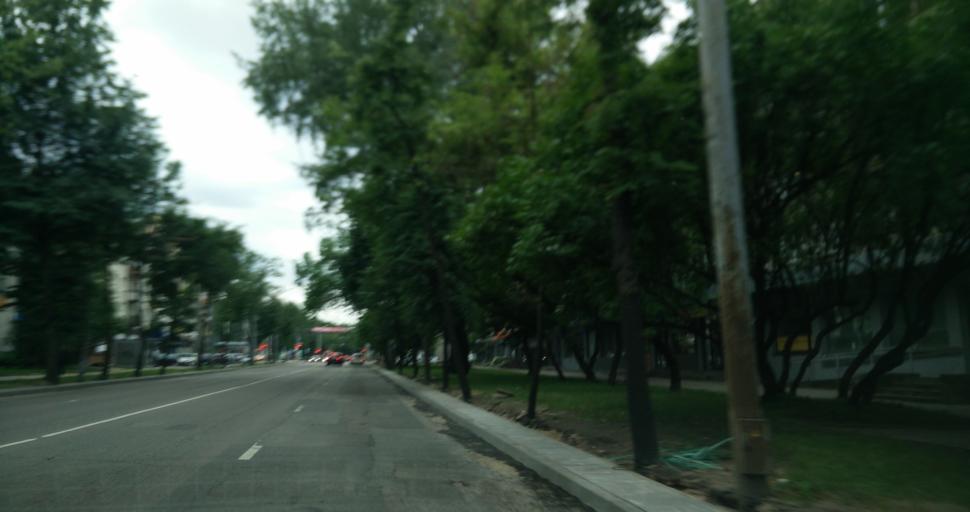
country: LT
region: Vilnius County
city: Rasos
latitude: 54.7131
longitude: 25.3153
